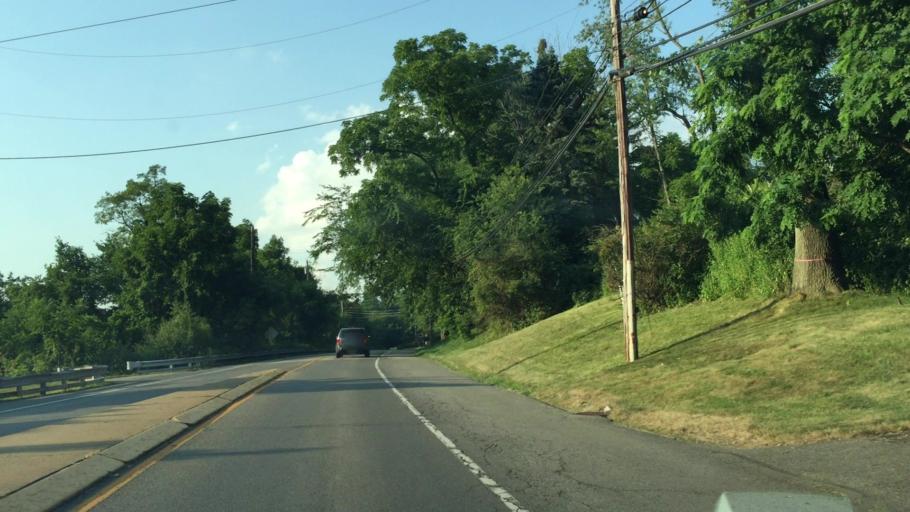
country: US
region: Pennsylvania
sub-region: Allegheny County
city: Bryn Mawr
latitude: 40.3138
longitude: -80.0886
